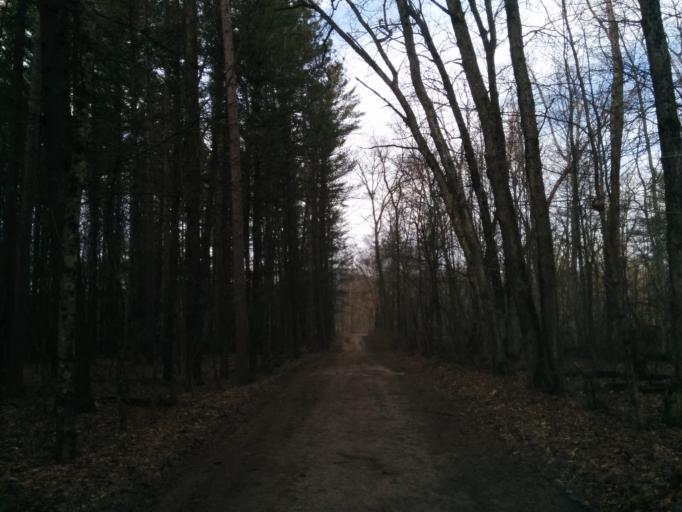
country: US
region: Michigan
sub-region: Newaygo County
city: Newaygo
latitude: 43.4168
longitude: -85.7261
